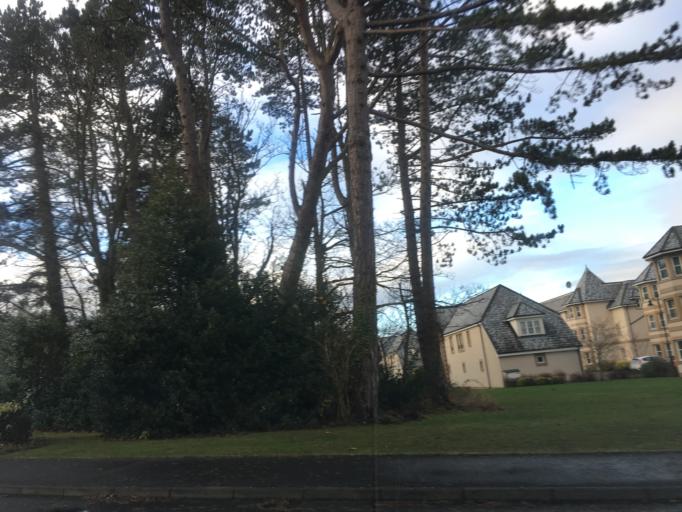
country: GB
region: Scotland
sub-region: Edinburgh
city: Colinton
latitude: 55.9141
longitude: -3.2248
